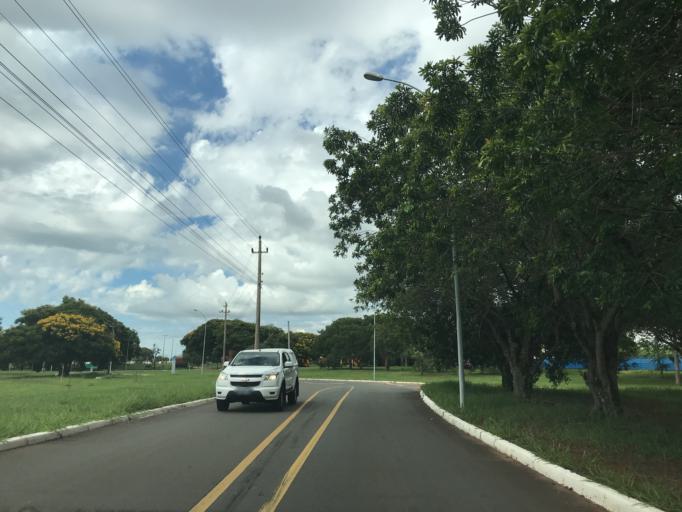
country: BR
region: Federal District
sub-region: Brasilia
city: Brasilia
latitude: -15.8076
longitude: -47.8780
